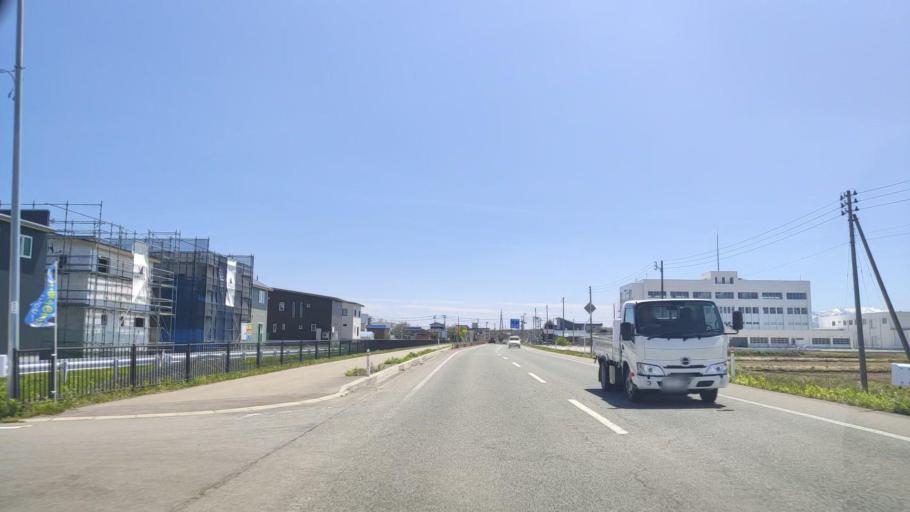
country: JP
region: Yamagata
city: Shinjo
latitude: 38.7533
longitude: 140.2946
